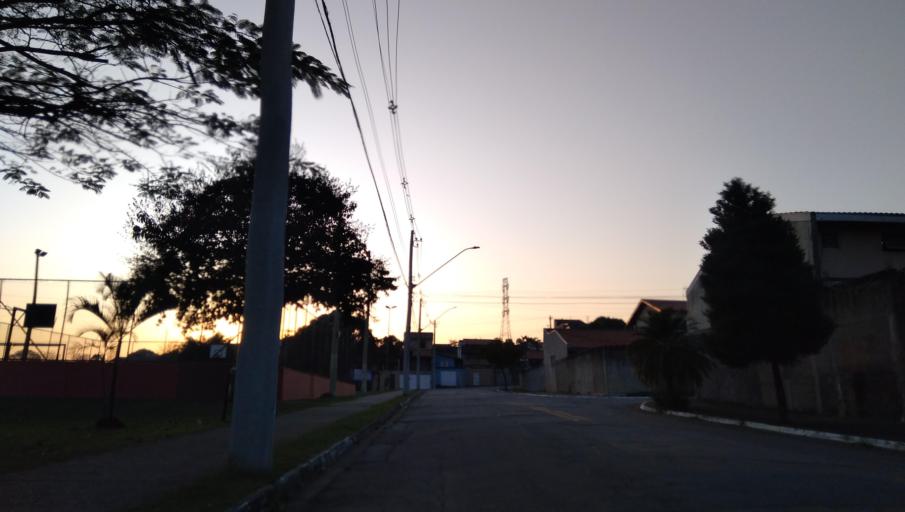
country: BR
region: Sao Paulo
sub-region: Sao Jose Dos Campos
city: Sao Jose dos Campos
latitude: -23.1764
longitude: -45.8183
